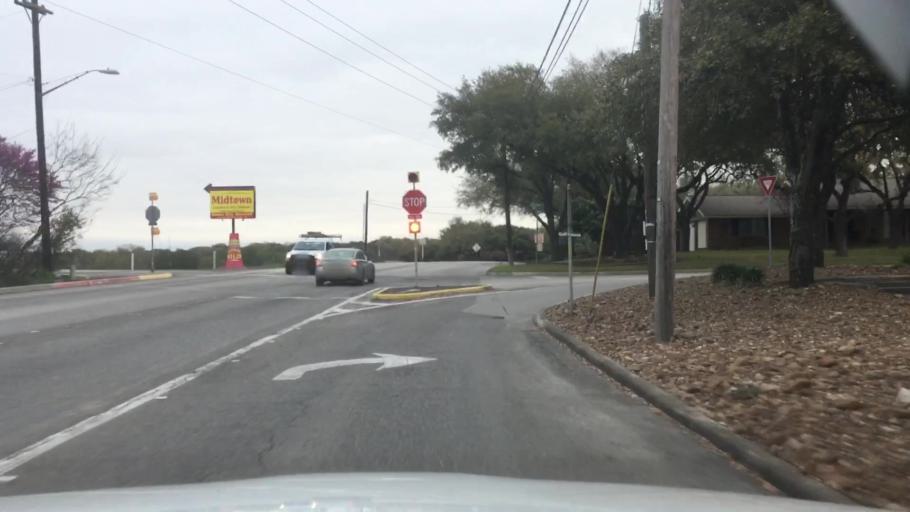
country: US
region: Texas
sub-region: Bexar County
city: Windcrest
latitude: 29.5230
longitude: -98.3820
